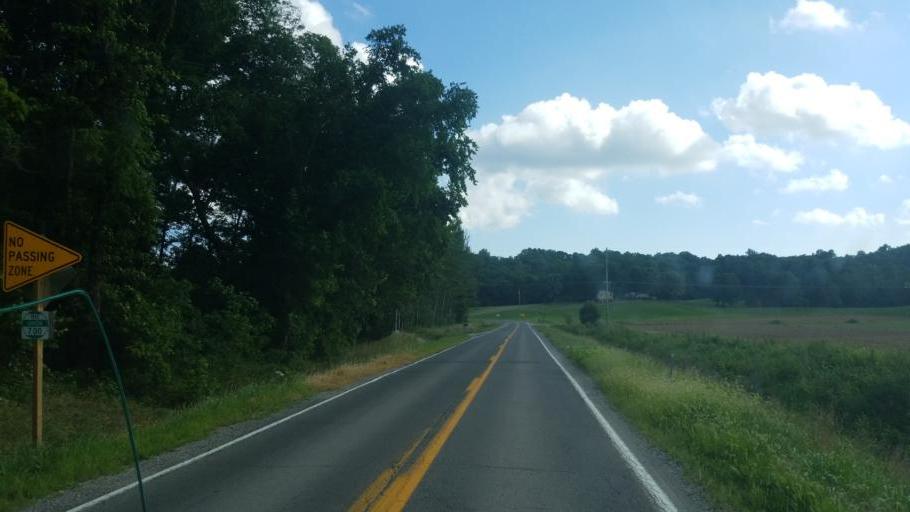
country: US
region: Illinois
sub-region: Union County
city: Cobden
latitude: 37.5494
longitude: -89.2651
